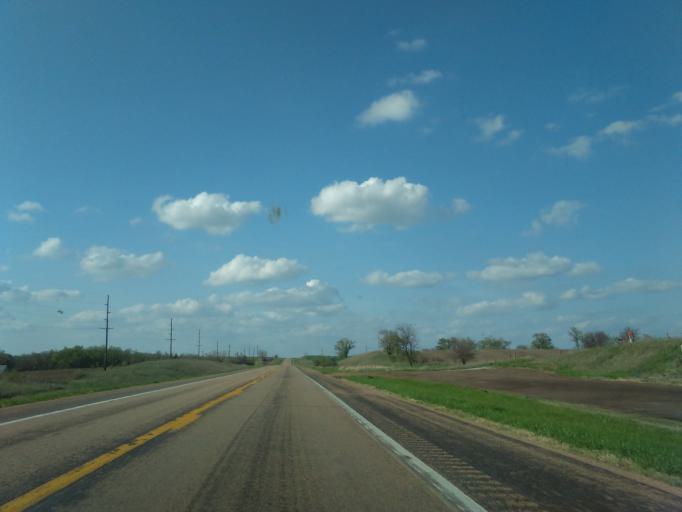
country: US
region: Nebraska
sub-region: Webster County
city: Red Cloud
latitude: 40.1100
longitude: -98.5188
